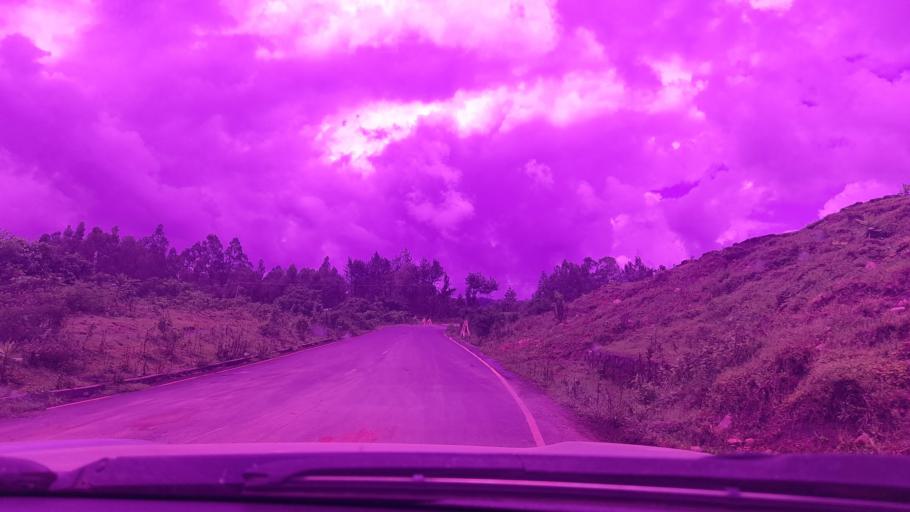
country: ET
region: Oromiya
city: Metu
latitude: 8.3286
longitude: 35.7596
